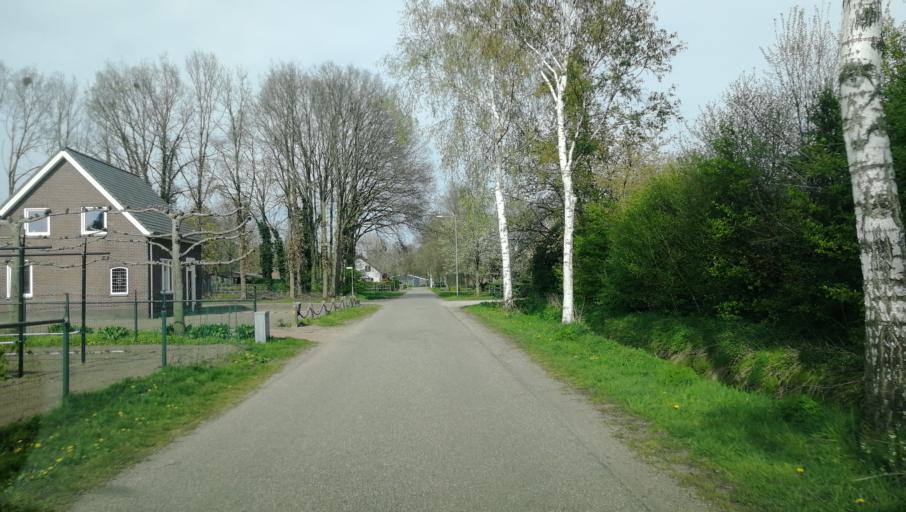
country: NL
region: Limburg
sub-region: Gemeente Peel en Maas
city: Maasbree
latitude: 51.3667
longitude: 6.0811
